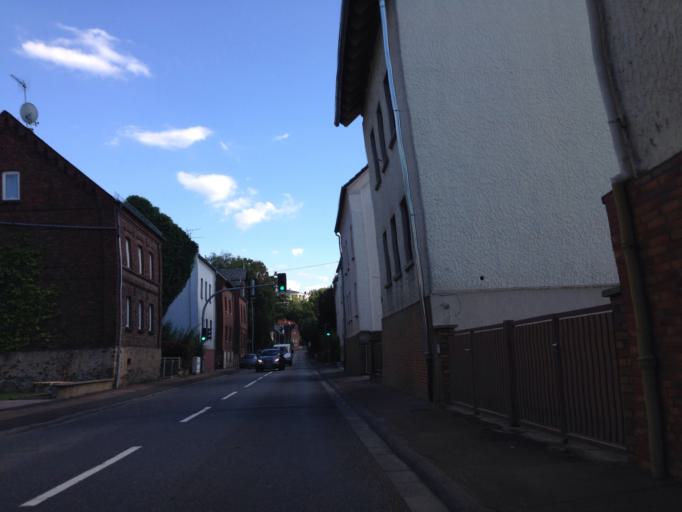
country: DE
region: Hesse
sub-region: Regierungsbezirk Giessen
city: Steeden
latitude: 50.4150
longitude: 8.1274
